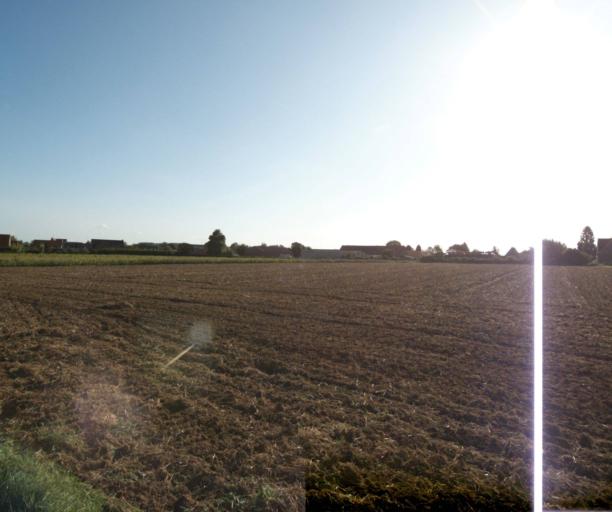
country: FR
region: Nord-Pas-de-Calais
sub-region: Departement du Nord
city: Sainghin-en-Melantois
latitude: 50.5811
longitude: 3.1847
